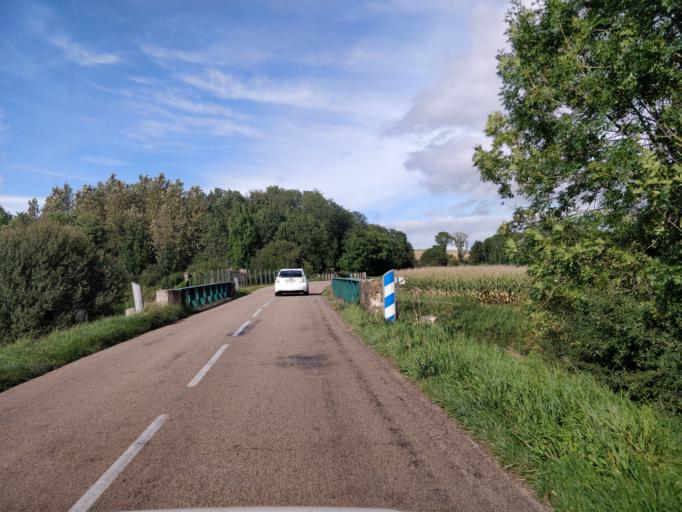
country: FR
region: Champagne-Ardenne
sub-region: Departement de l'Aube
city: Aix-en-Othe
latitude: 48.2277
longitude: 3.6196
